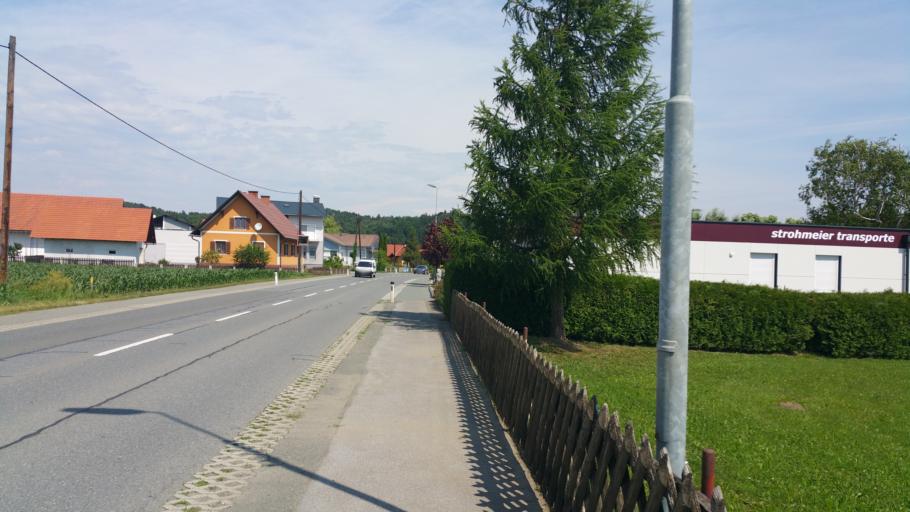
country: AT
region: Styria
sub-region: Politischer Bezirk Leibnitz
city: Pistorf
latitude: 46.7647
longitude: 15.3731
